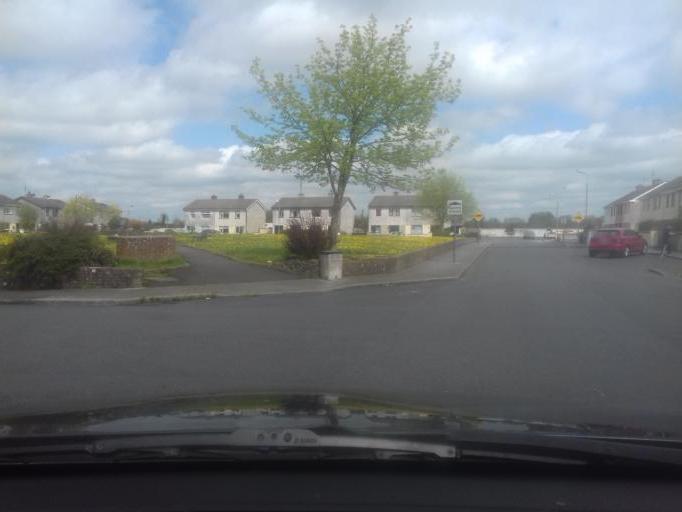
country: IE
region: Leinster
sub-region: Laois
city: Portlaoise
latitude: 53.0423
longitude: -7.3092
